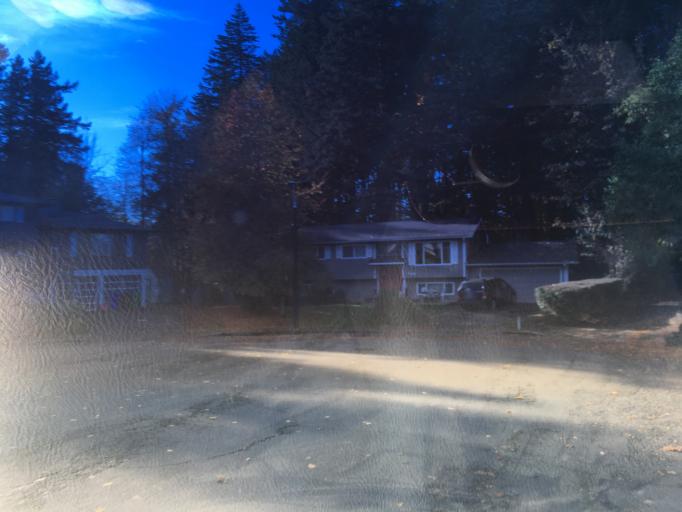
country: US
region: Oregon
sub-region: Multnomah County
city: Gresham
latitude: 45.5011
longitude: -122.3972
